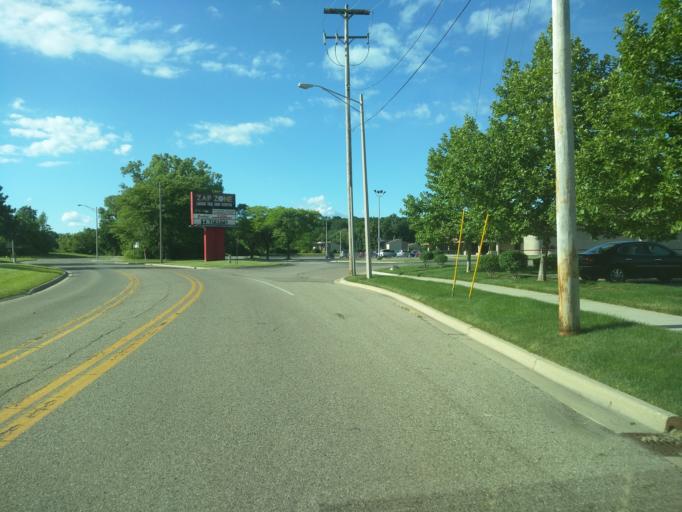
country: US
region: Michigan
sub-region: Eaton County
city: Waverly
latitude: 42.7430
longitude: -84.6194
